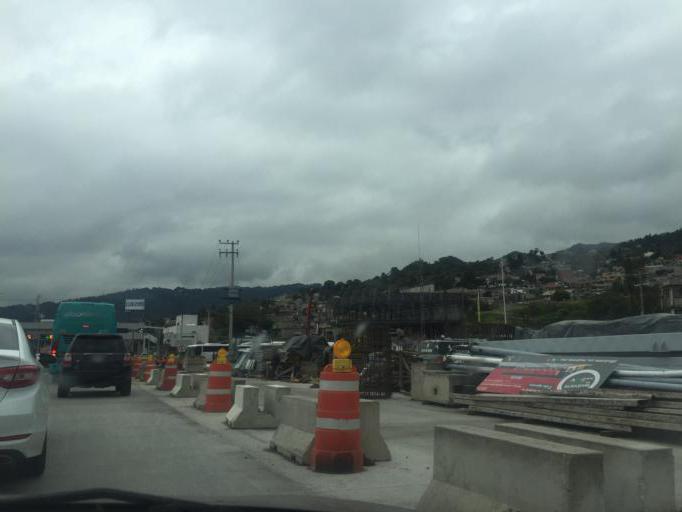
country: MX
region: Mexico City
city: Xochimilco
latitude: 19.2433
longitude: -99.1492
